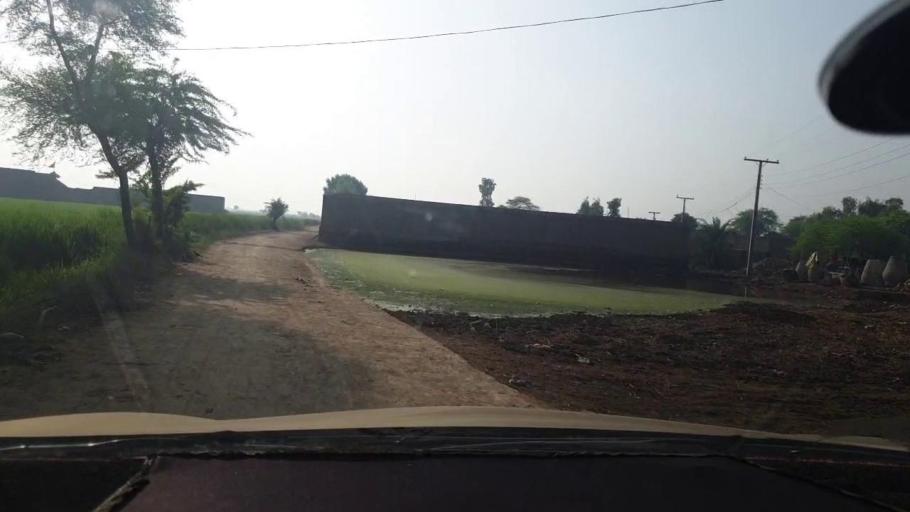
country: PK
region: Sindh
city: Kambar
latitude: 27.5355
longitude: 68.0193
